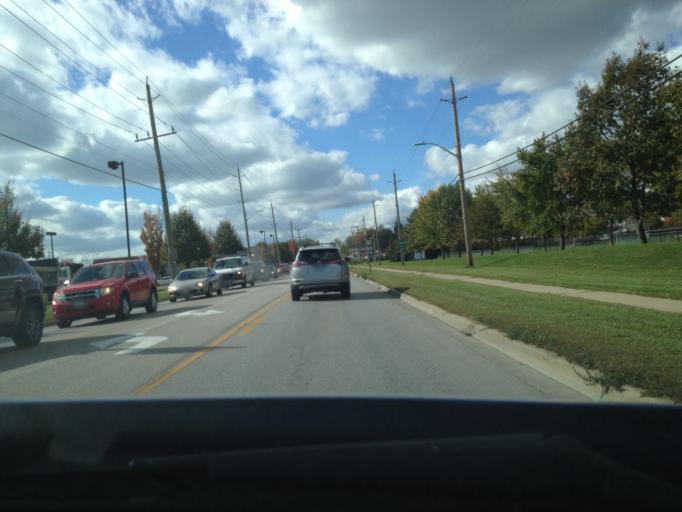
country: CA
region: Ontario
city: Amherstburg
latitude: 42.0337
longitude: -82.5943
